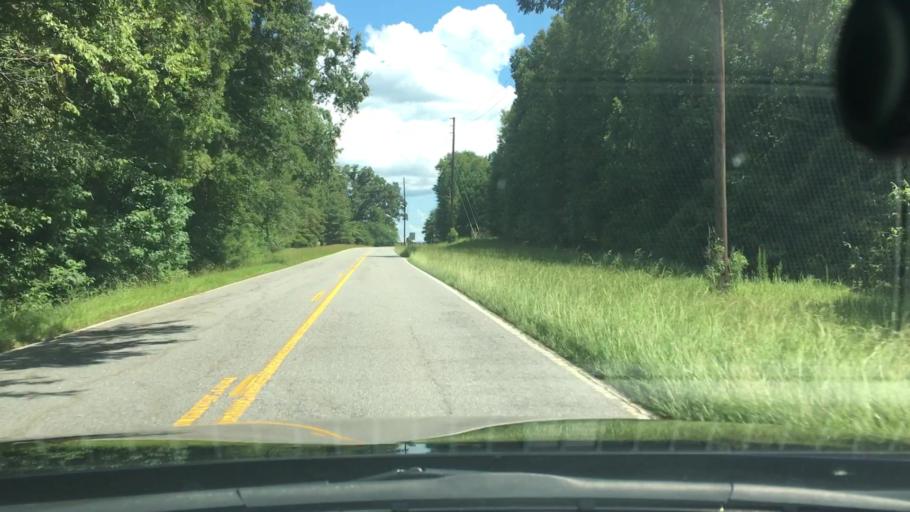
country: US
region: Georgia
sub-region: Putnam County
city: Jefferson
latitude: 33.3790
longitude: -83.2514
